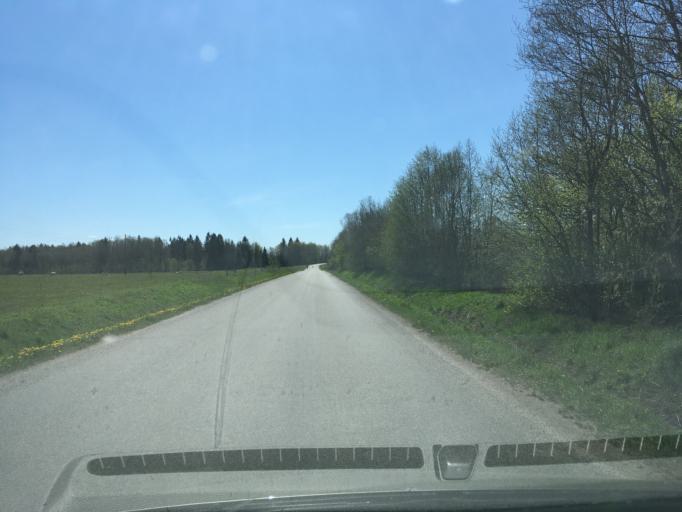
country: EE
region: Harju
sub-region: Raasiku vald
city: Arukula
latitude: 59.3805
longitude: 25.0776
